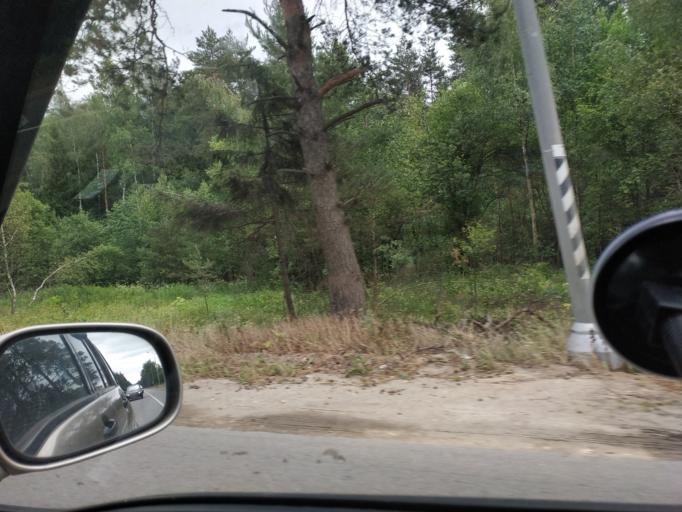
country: RU
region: Moskovskaya
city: Krasnoarmeysk
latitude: 56.0121
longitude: 38.1514
